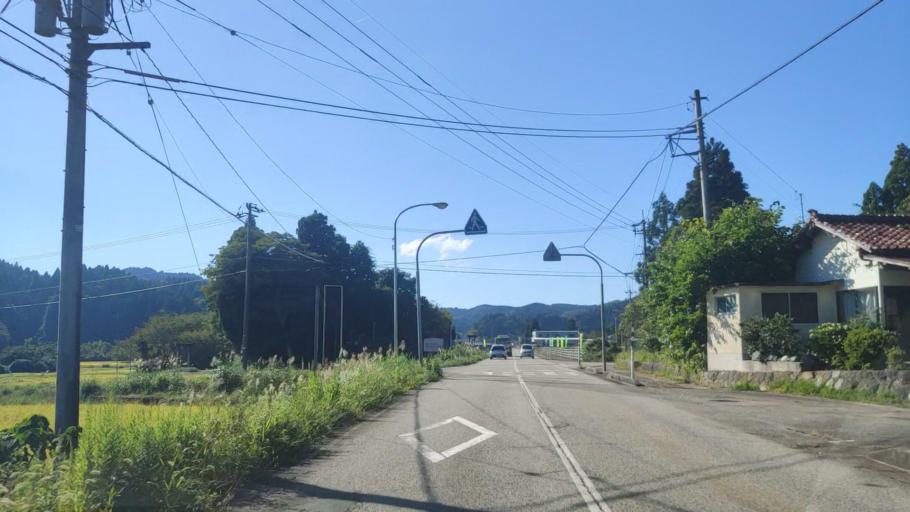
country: JP
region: Ishikawa
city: Nanao
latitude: 37.2791
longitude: 137.0490
